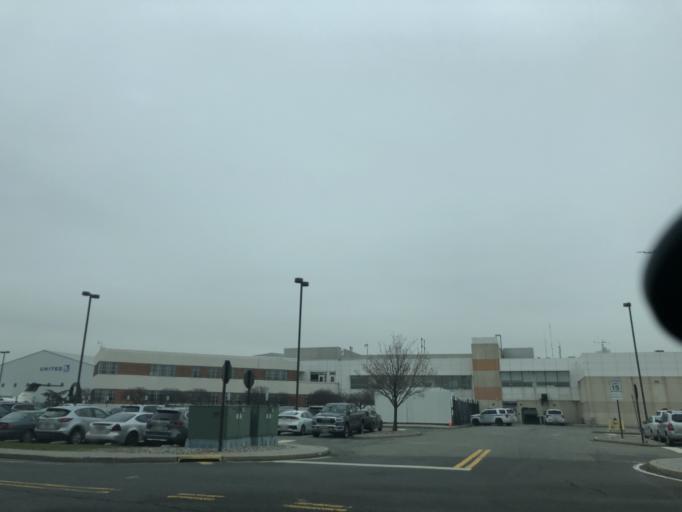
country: US
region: New Jersey
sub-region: Essex County
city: Newark
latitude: 40.7048
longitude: -74.1715
